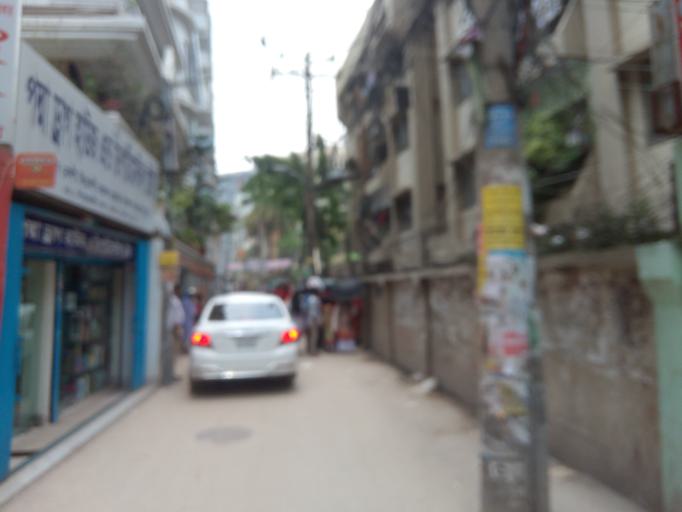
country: BD
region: Dhaka
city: Paltan
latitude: 23.7440
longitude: 90.4111
